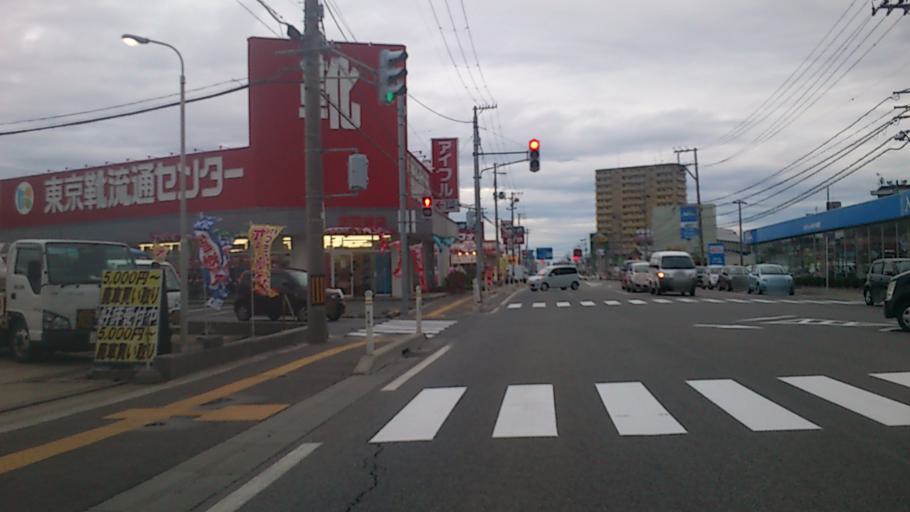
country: JP
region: Akita
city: Akita Shi
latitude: 39.7389
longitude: 140.0962
